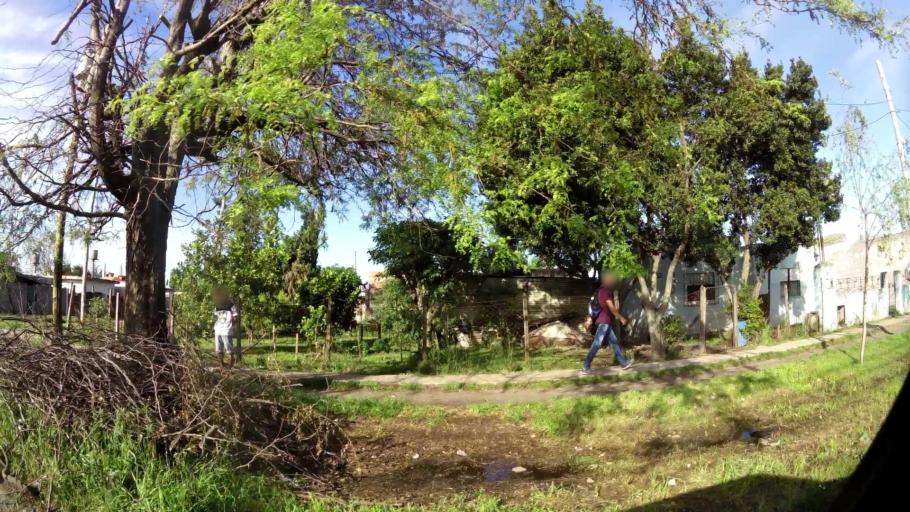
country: AR
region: Buenos Aires
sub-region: Partido de Almirante Brown
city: Adrogue
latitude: -34.8153
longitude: -58.3255
